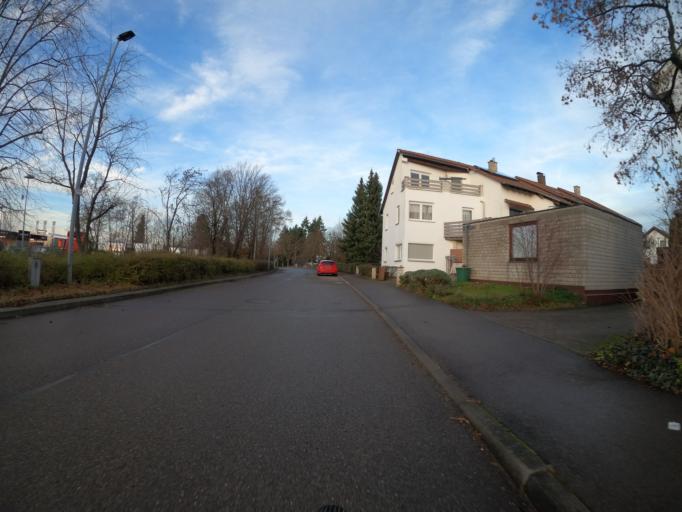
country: DE
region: Baden-Wuerttemberg
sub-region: Regierungsbezirk Stuttgart
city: Zell unter Aichelberg
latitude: 48.6536
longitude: 9.5745
